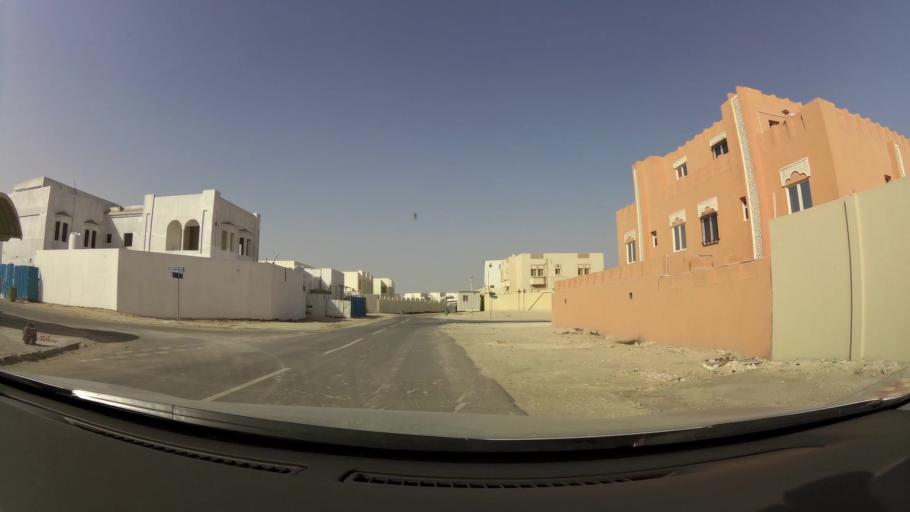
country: QA
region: Baladiyat ar Rayyan
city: Ar Rayyan
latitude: 25.3445
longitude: 51.4226
